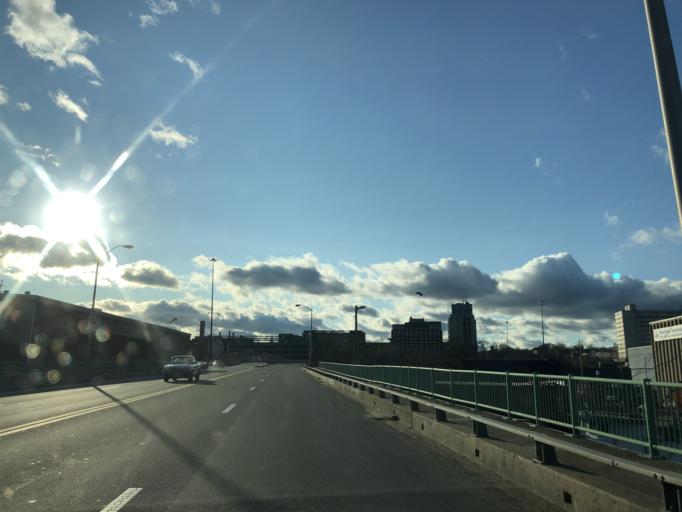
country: US
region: Massachusetts
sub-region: Bristol County
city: New Bedford
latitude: 41.6382
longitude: -70.9208
